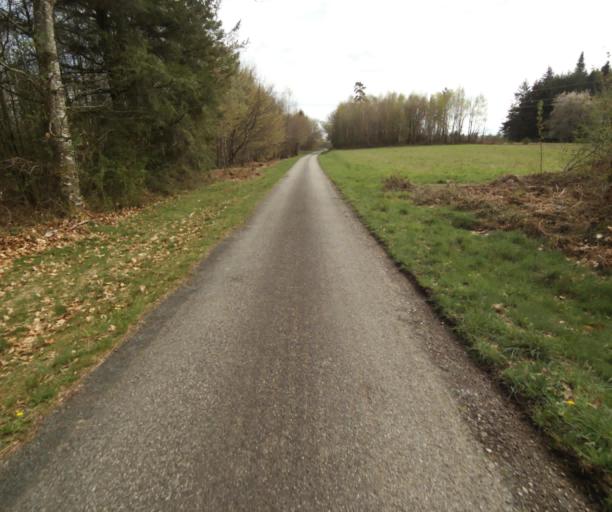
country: FR
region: Limousin
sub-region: Departement de la Correze
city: Argentat
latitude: 45.1942
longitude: 1.9106
